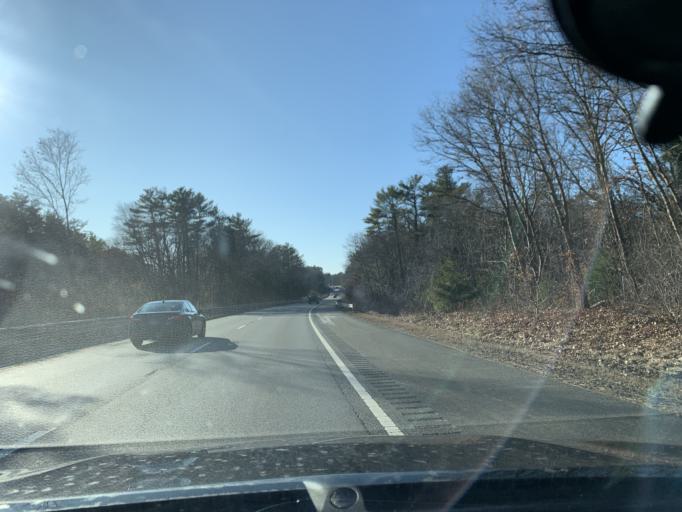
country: US
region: Massachusetts
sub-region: Essex County
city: Beverly Cove
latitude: 42.5792
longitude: -70.8269
